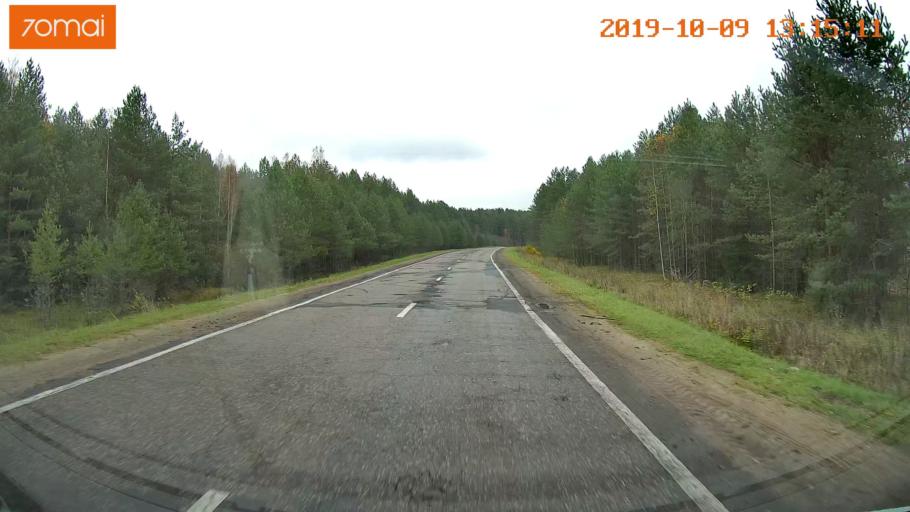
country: RU
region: Jaroslavl
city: Lyubim
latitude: 58.3682
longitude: 40.7475
